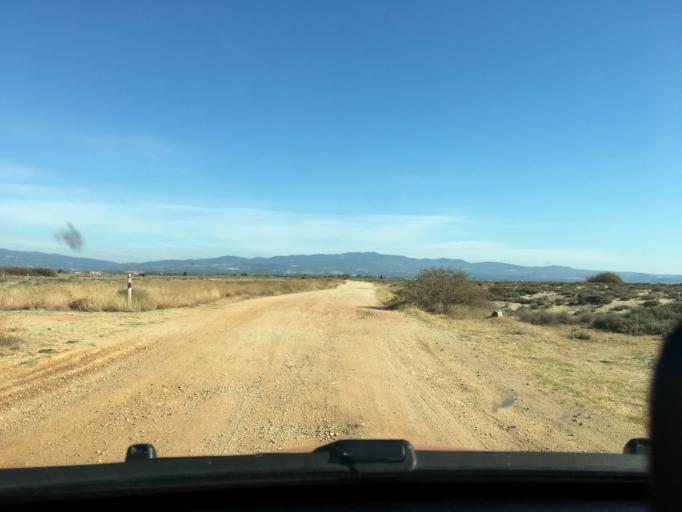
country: GR
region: Central Macedonia
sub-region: Nomos Chalkidikis
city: Nea Potidhaia
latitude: 40.2299
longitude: 23.3397
